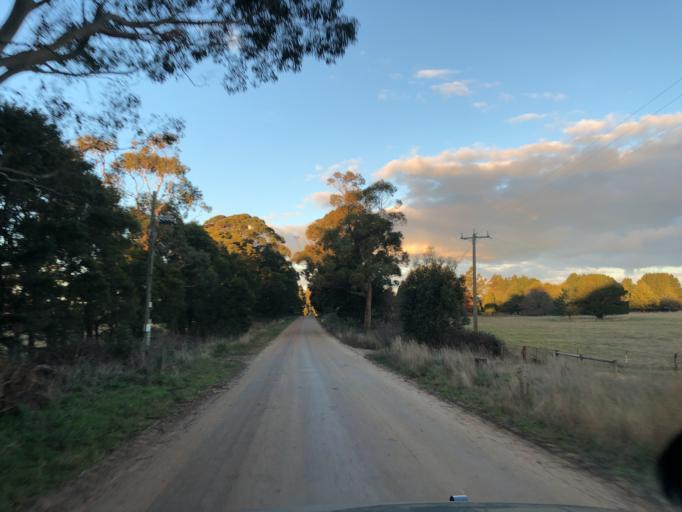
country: AU
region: Victoria
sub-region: Moorabool
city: Bacchus Marsh
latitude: -37.4069
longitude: 144.3697
